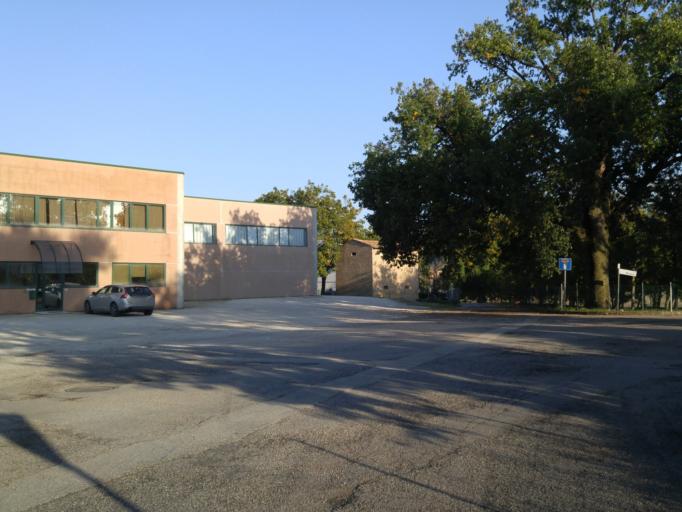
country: IT
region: The Marches
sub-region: Provincia di Pesaro e Urbino
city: Tavernelle
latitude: 43.7153
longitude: 12.8631
